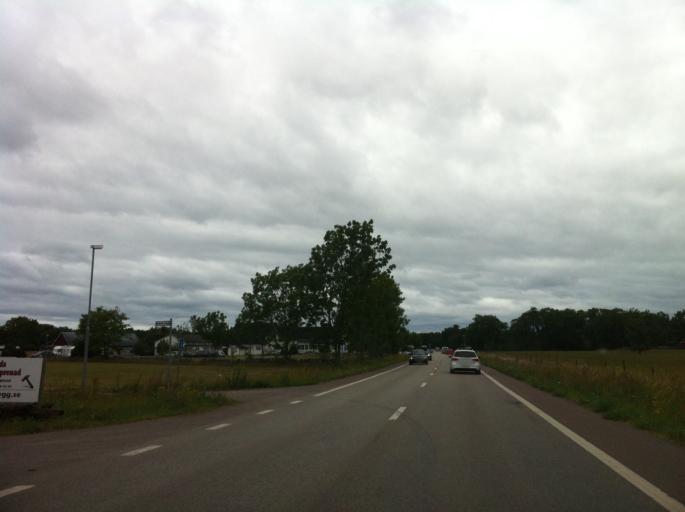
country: SE
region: Kalmar
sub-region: Borgholms Kommun
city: Borgholm
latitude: 57.2494
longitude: 17.0574
